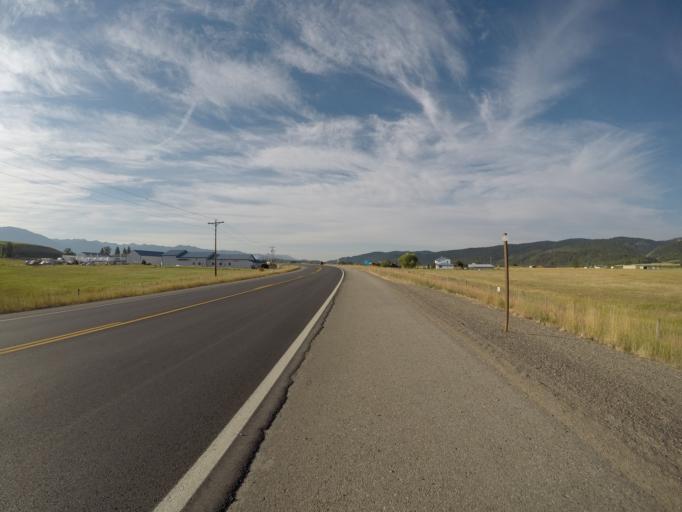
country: US
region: Wyoming
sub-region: Lincoln County
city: Afton
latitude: 42.9295
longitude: -111.0074
